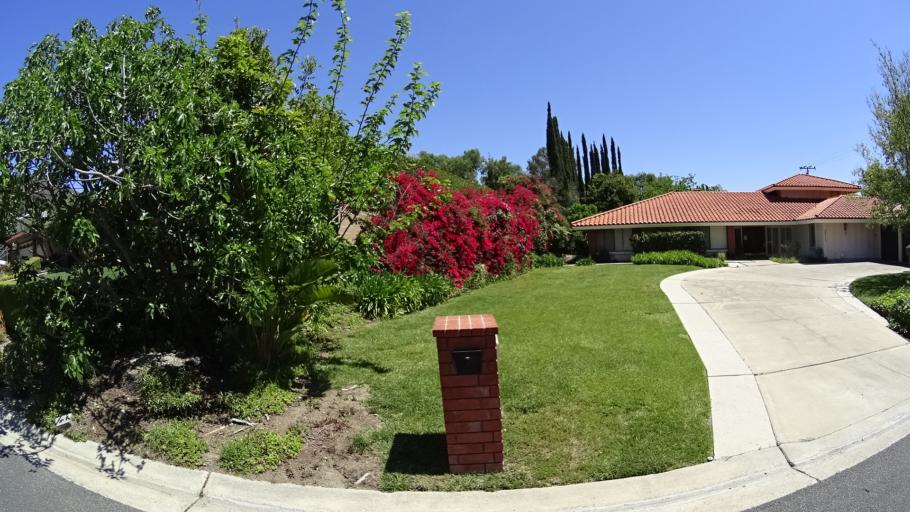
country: US
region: California
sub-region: Orange County
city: Villa Park
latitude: 33.8271
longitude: -117.8033
